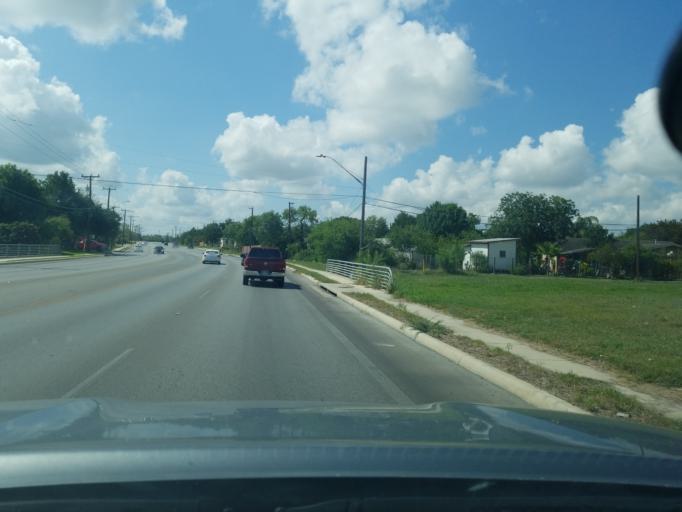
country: US
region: Texas
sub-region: Bexar County
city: San Antonio
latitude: 29.3349
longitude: -98.5342
